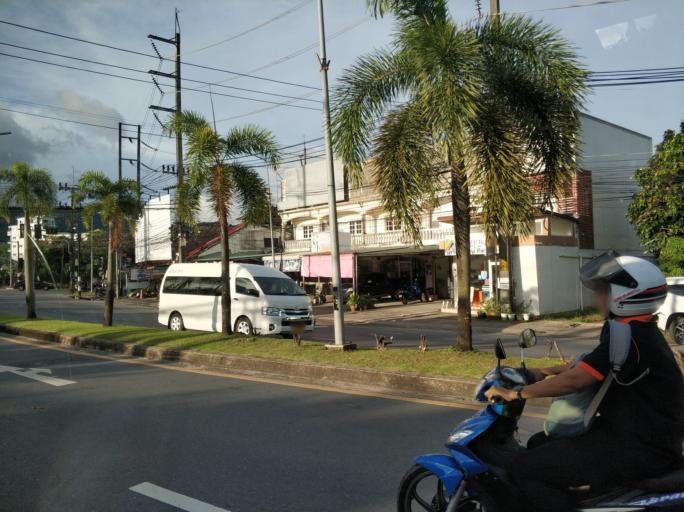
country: TH
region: Phuket
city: Kathu
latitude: 7.9100
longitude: 98.3341
